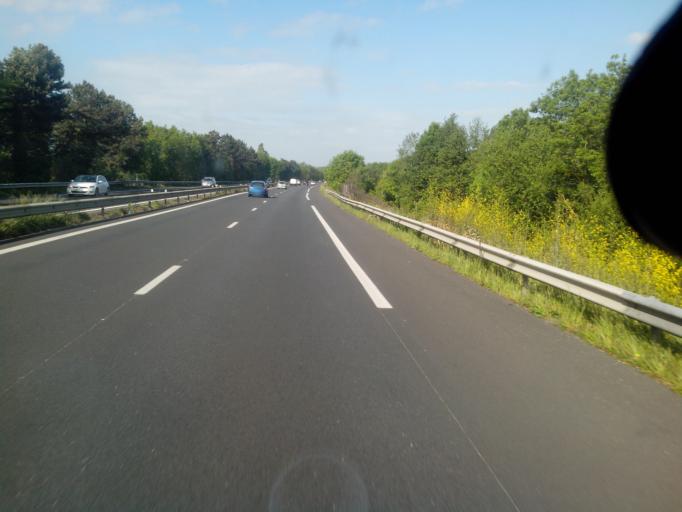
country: FR
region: Lower Normandy
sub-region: Departement du Calvados
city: Troarn
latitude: 49.2002
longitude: -0.1774
